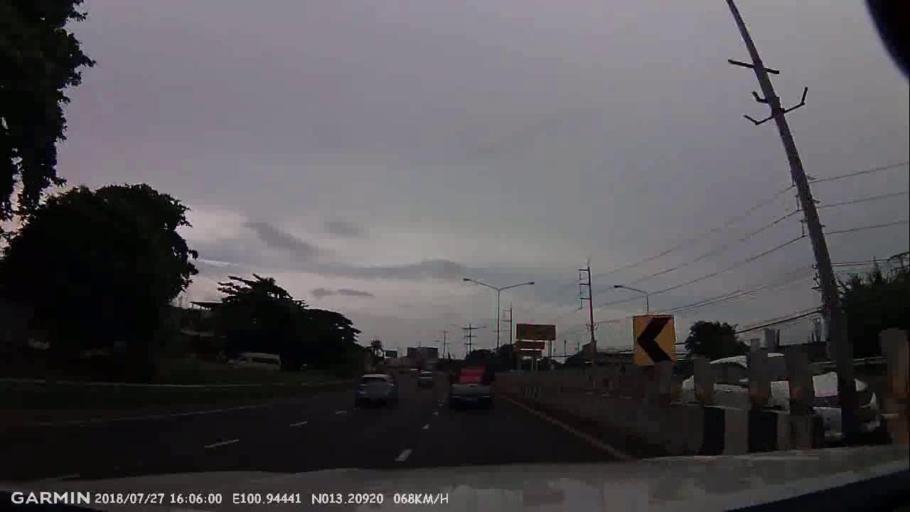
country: TH
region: Chon Buri
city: Si Racha
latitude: 13.2094
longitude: 100.9443
